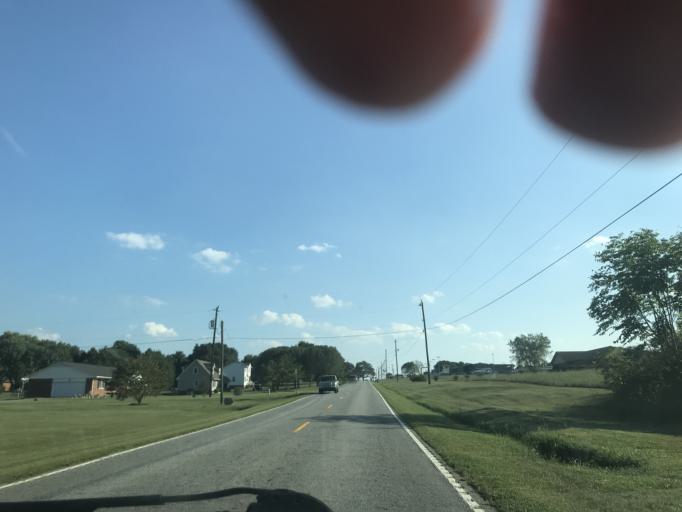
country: US
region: South Carolina
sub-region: Cherokee County
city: Gaffney
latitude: 35.1080
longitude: -81.6809
